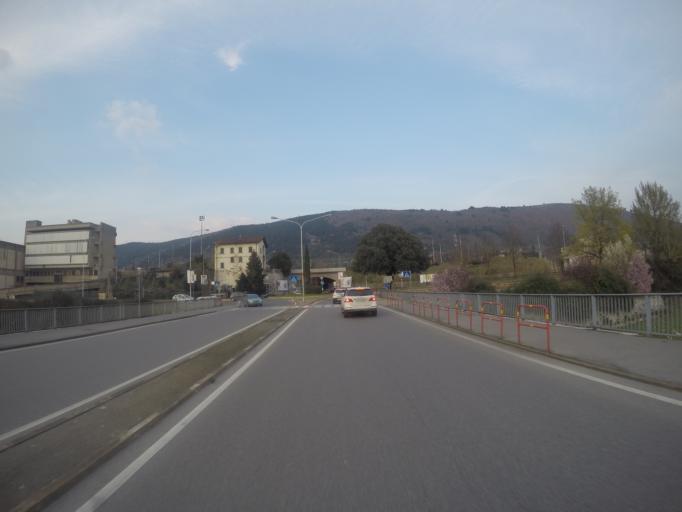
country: IT
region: Tuscany
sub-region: Provincia di Prato
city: Prato
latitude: 43.8720
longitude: 11.1158
